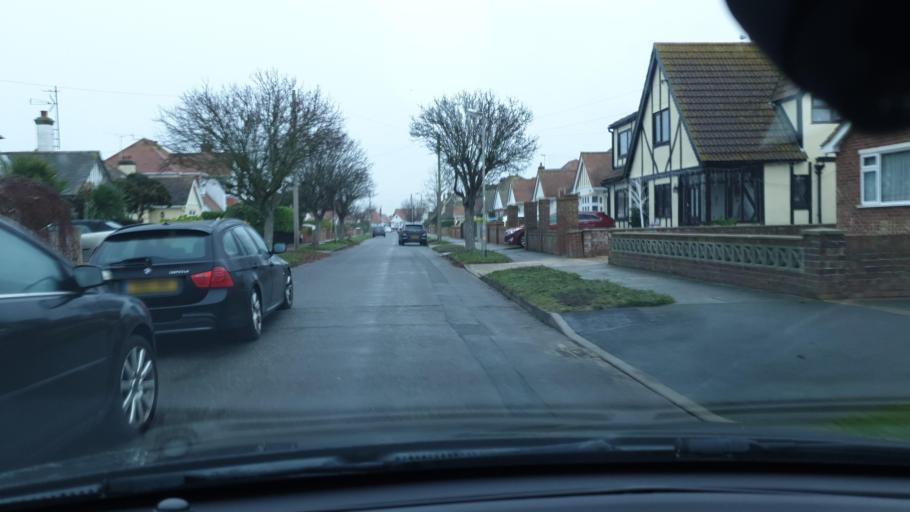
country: GB
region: England
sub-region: Essex
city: Clacton-on-Sea
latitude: 51.8011
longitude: 1.1879
